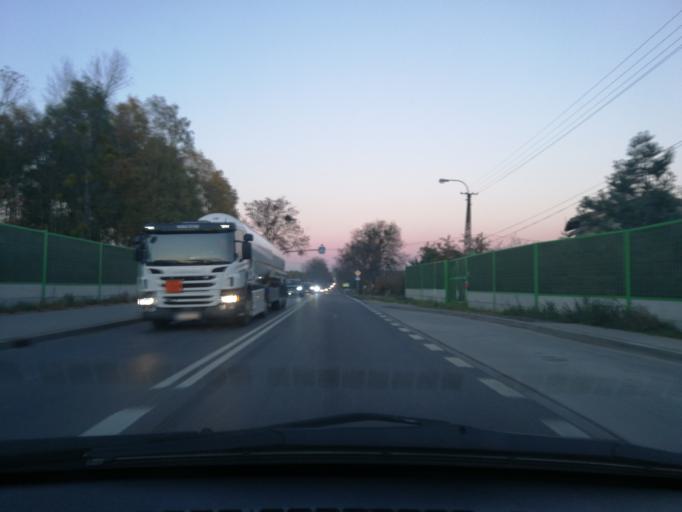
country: PL
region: Lodz Voivodeship
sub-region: Powiat lodzki wschodni
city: Andrespol
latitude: 51.7943
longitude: 19.6248
